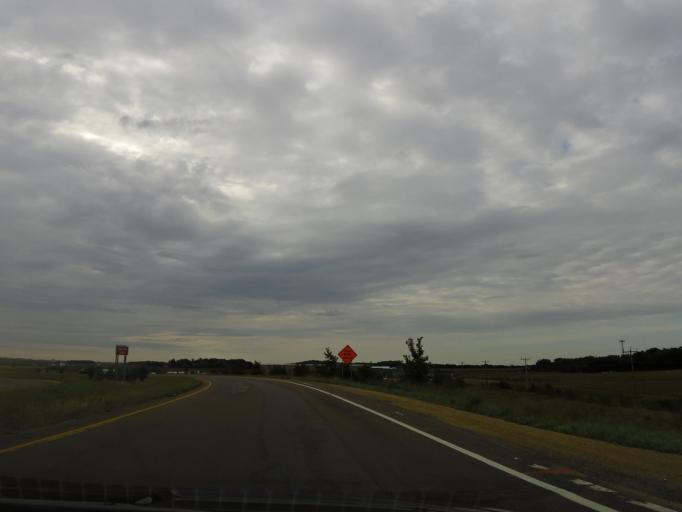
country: US
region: Minnesota
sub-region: Dakota County
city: Rosemount
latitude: 44.7101
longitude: -93.0347
